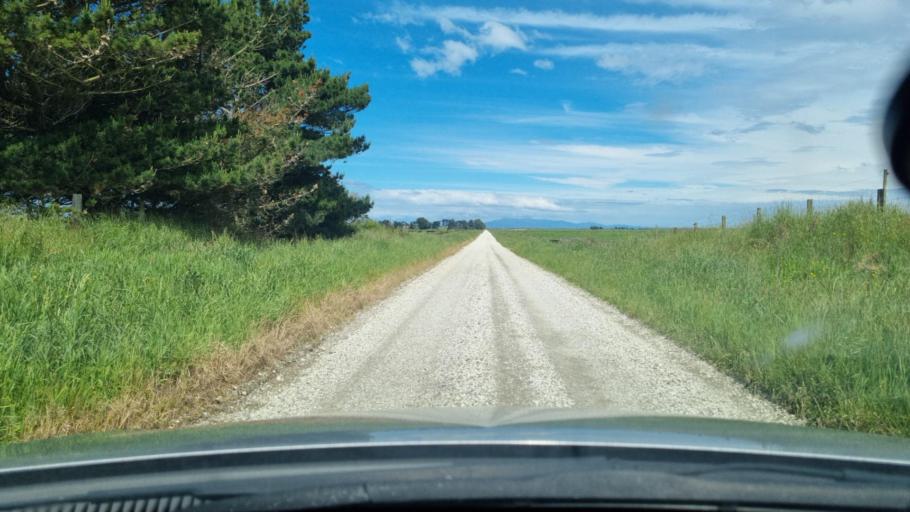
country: NZ
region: Southland
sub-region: Invercargill City
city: Invercargill
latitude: -46.3749
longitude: 168.2750
